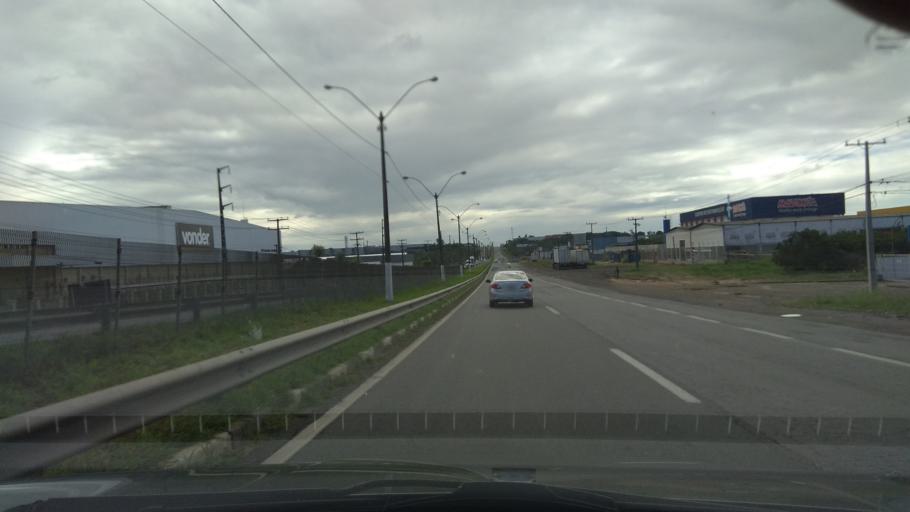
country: BR
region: Bahia
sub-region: Feira De Santana
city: Feira de Santana
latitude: -12.2896
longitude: -38.9126
